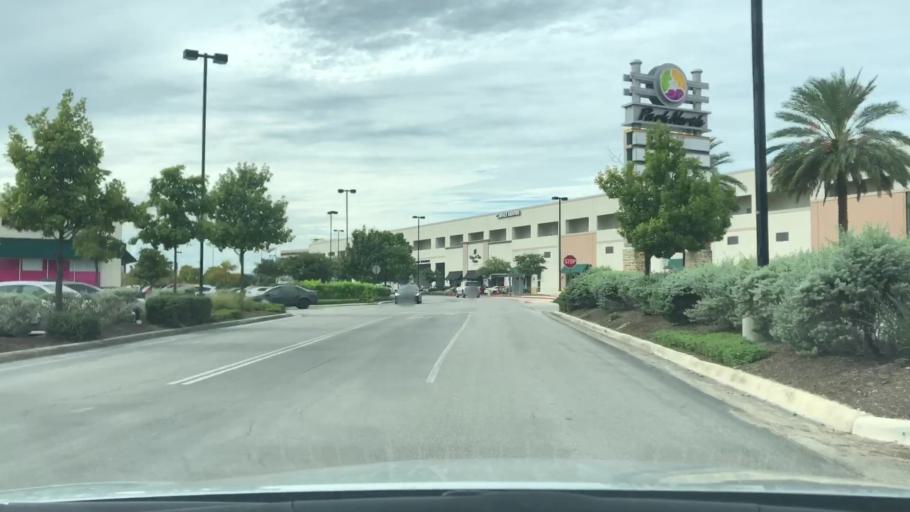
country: US
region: Texas
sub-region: Bexar County
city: Castle Hills
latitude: 29.5174
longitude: -98.5030
